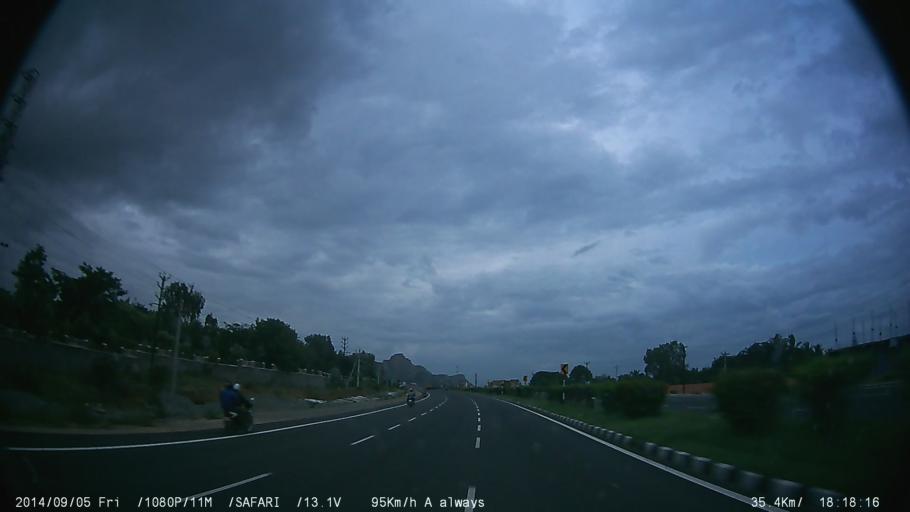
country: IN
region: Tamil Nadu
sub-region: Krishnagiri
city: Kelamangalam
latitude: 12.6678
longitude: 77.9930
